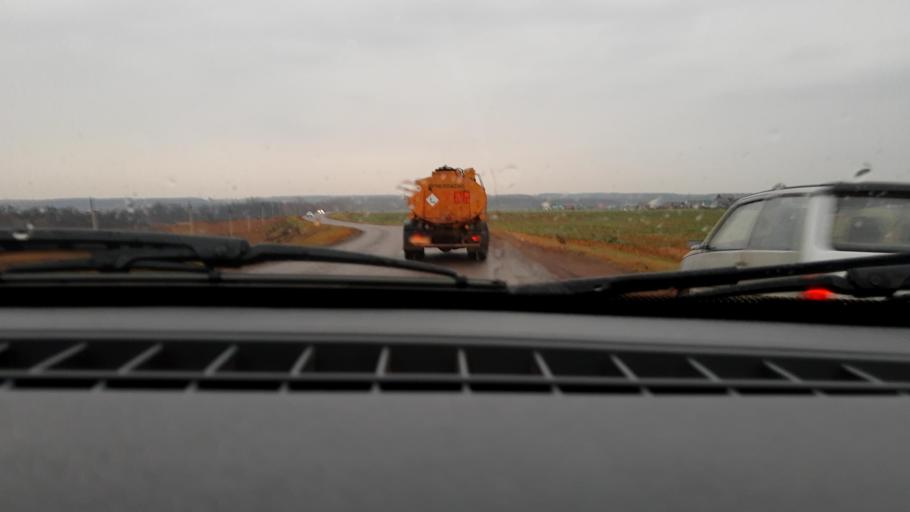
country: RU
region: Bashkortostan
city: Mikhaylovka
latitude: 54.8307
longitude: 55.9583
